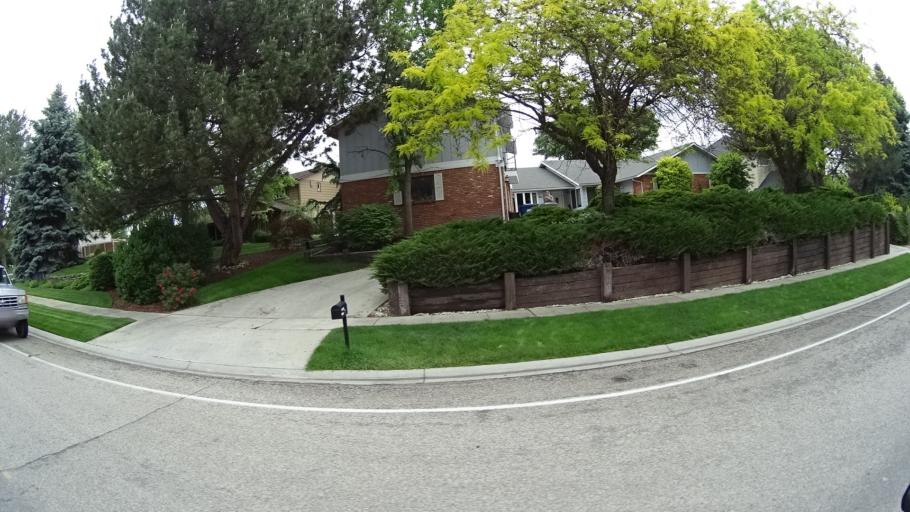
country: US
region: Idaho
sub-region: Ada County
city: Eagle
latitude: 43.7024
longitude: -116.3433
